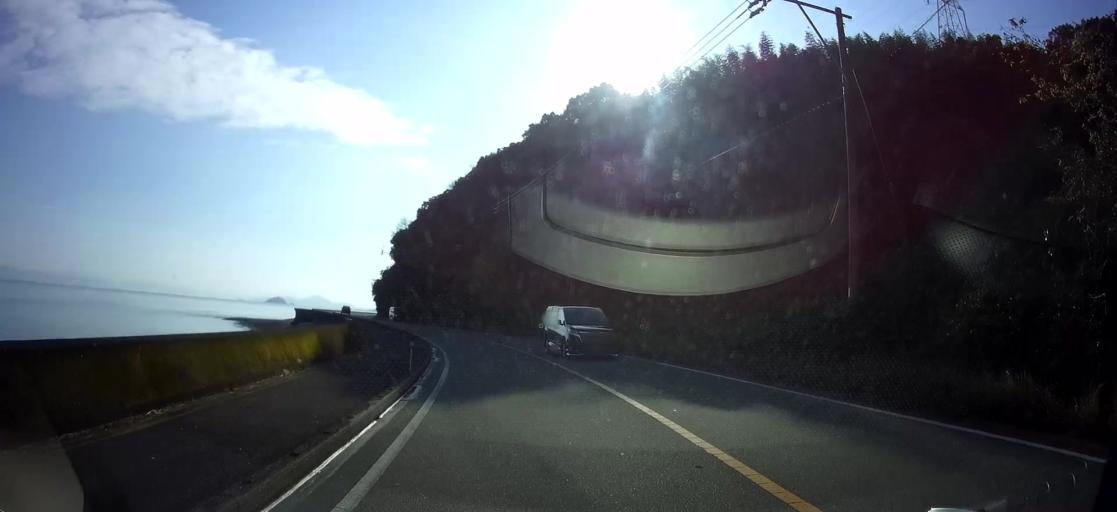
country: JP
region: Kumamoto
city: Yatsushiro
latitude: 32.5058
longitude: 130.4512
